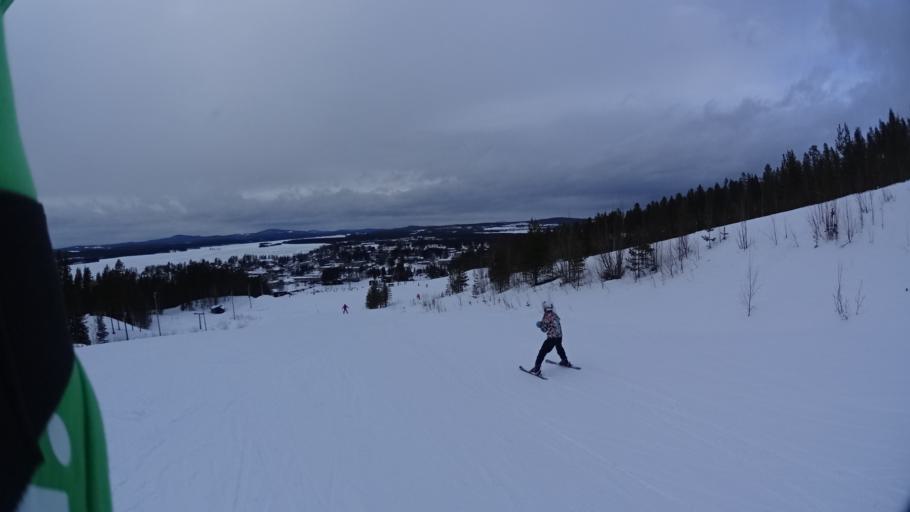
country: SE
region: Vaesterbotten
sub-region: Mala Kommun
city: Mala
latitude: 65.1789
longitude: 18.7577
